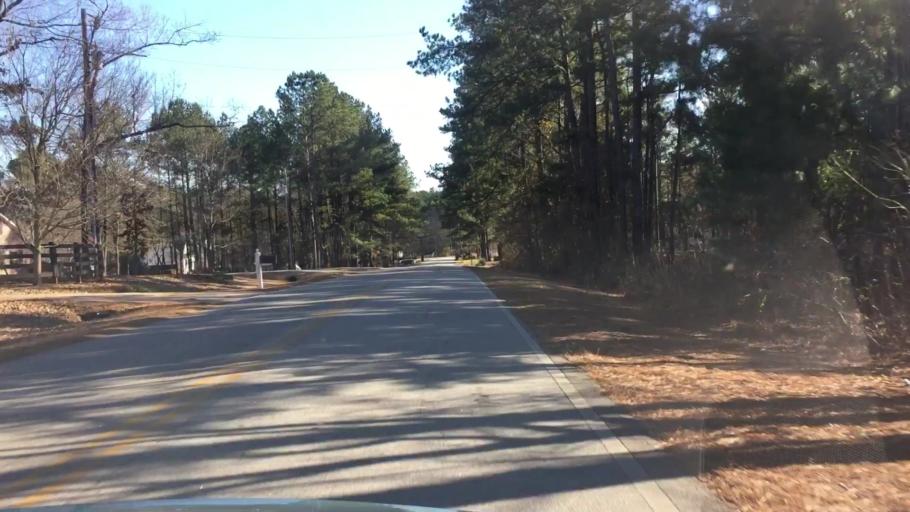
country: US
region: Georgia
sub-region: Henry County
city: McDonough
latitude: 33.4980
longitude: -84.0723
